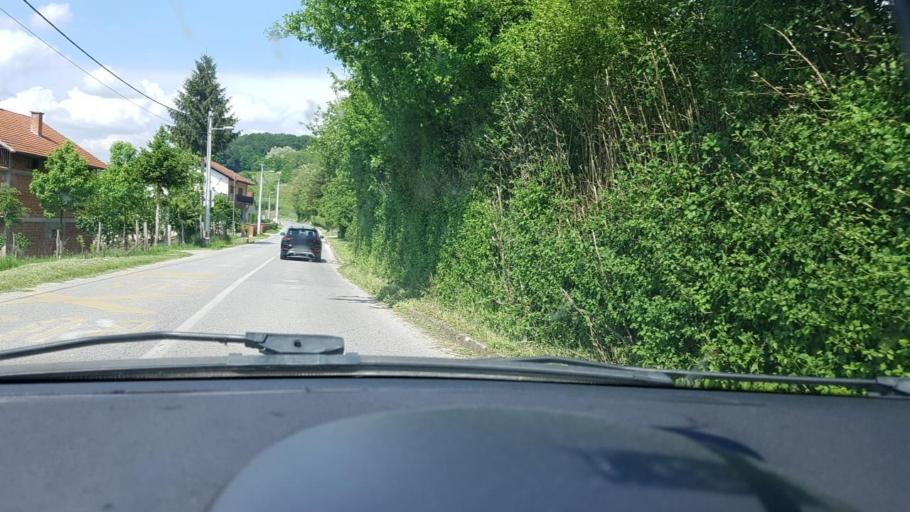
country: HR
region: Grad Zagreb
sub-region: Sesvete
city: Sesvete
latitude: 45.9122
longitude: 16.1678
